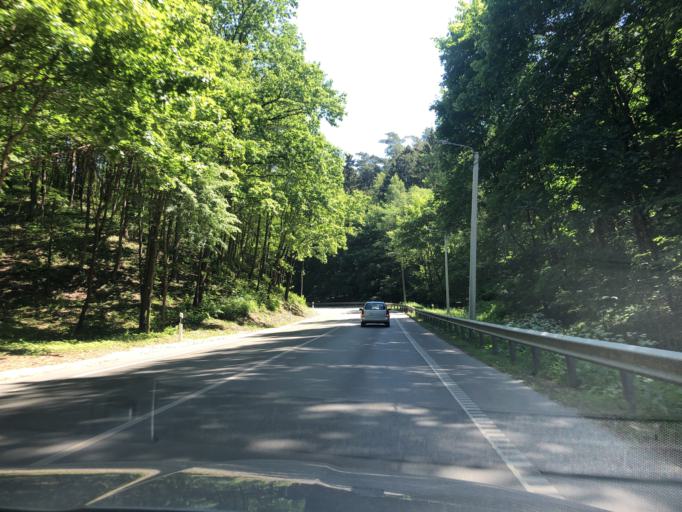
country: LT
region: Kauno apskritis
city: Dainava (Kaunas)
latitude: 54.8704
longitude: 23.9834
